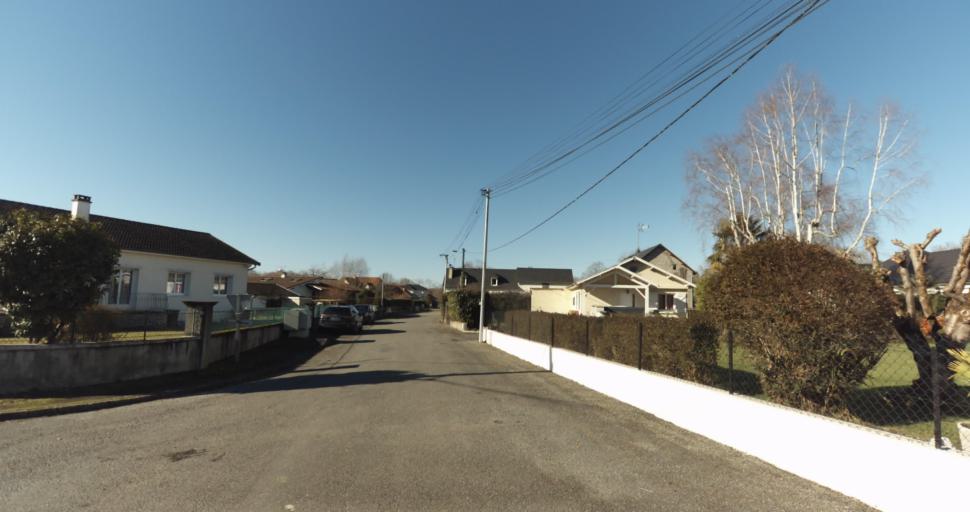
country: FR
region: Aquitaine
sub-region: Departement des Pyrenees-Atlantiques
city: Buros
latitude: 43.3277
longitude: -0.2911
